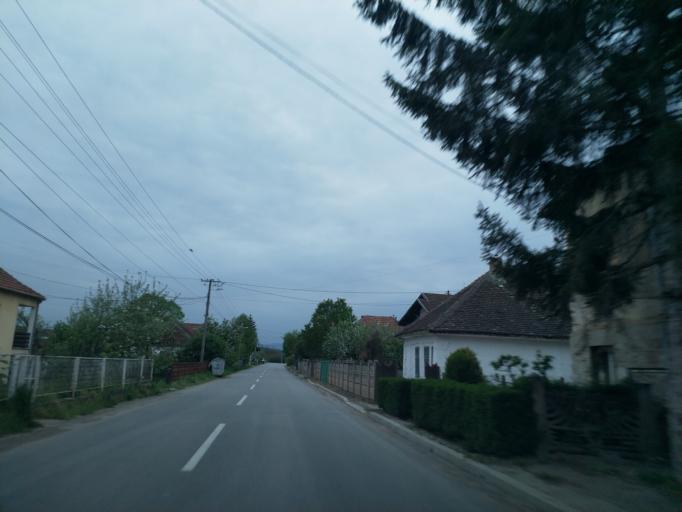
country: RS
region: Central Serbia
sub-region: Pomoravski Okrug
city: Cuprija
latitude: 43.9633
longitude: 21.4790
